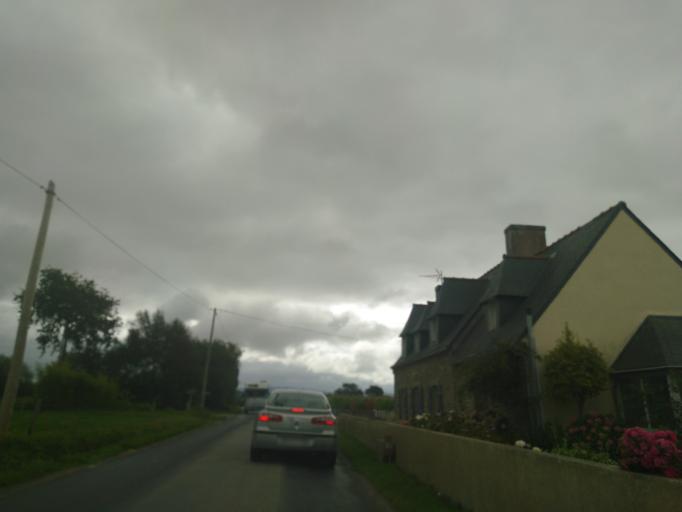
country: FR
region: Brittany
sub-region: Departement du Finistere
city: Plomodiern
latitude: 48.1577
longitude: -4.2469
